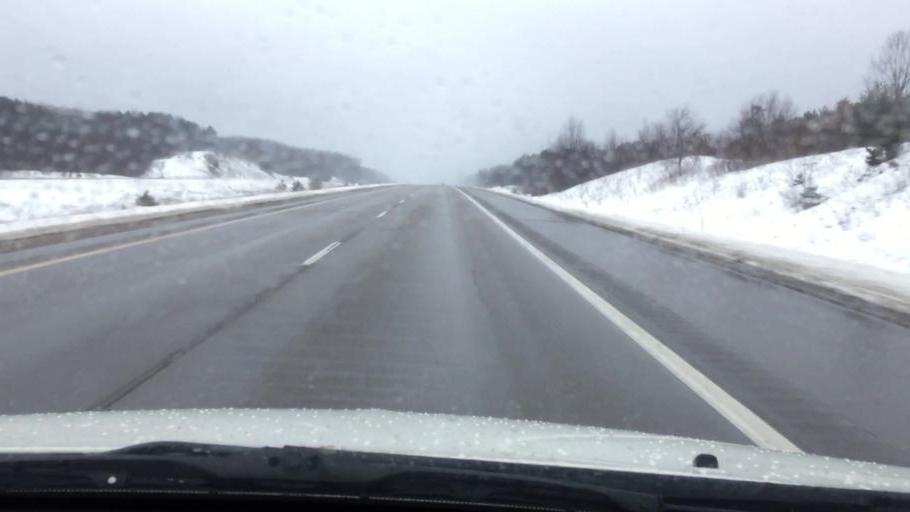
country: US
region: Michigan
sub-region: Wexford County
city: Manton
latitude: 44.3651
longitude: -85.4025
